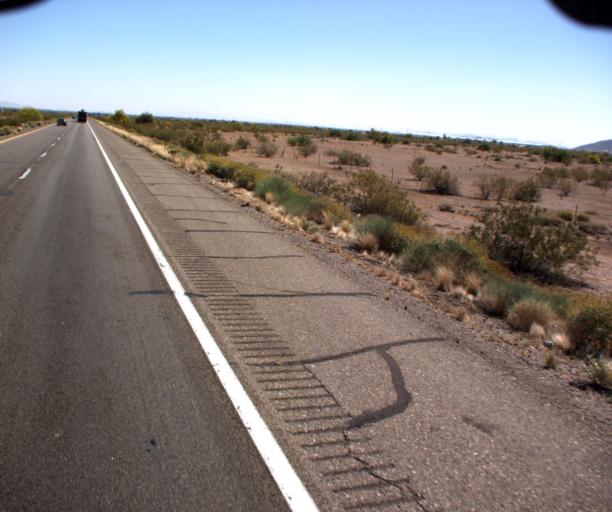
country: US
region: Arizona
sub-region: Maricopa County
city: Buckeye
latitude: 33.5028
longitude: -112.9664
